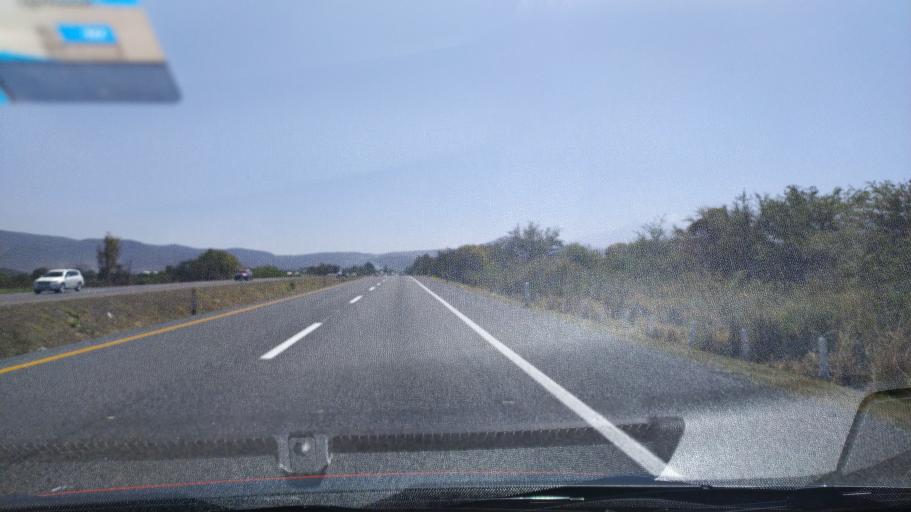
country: MX
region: Jalisco
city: Usmajac
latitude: 19.9155
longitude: -103.5272
